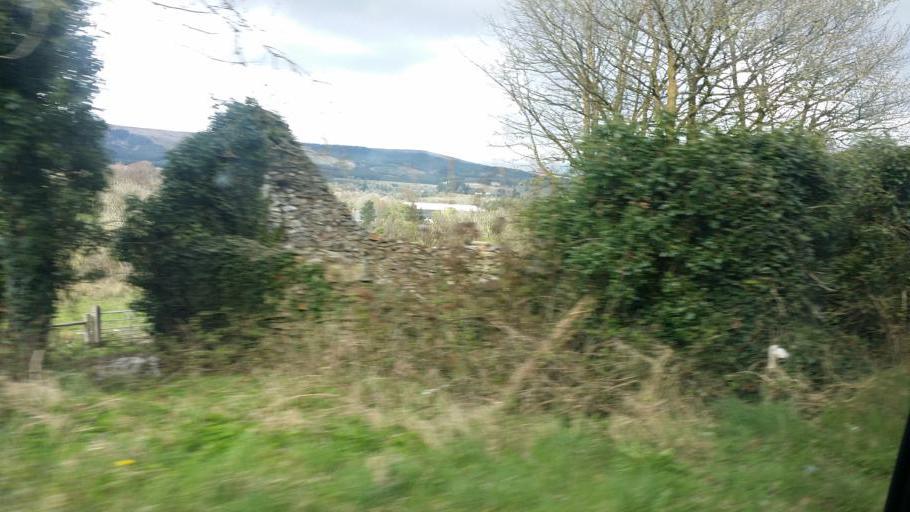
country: IE
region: Connaught
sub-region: County Leitrim
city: Manorhamilton
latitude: 54.3042
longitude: -8.1404
